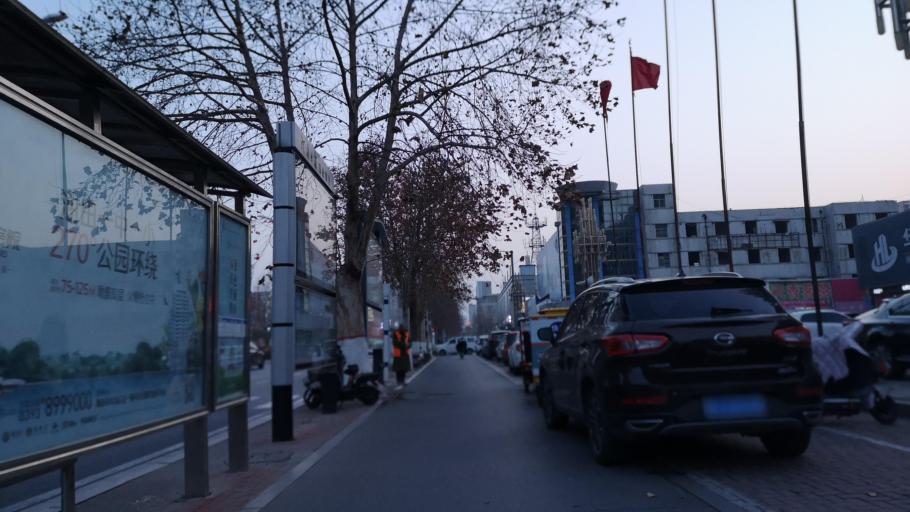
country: CN
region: Henan Sheng
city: Zhongyuanlu
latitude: 35.7752
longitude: 115.0704
